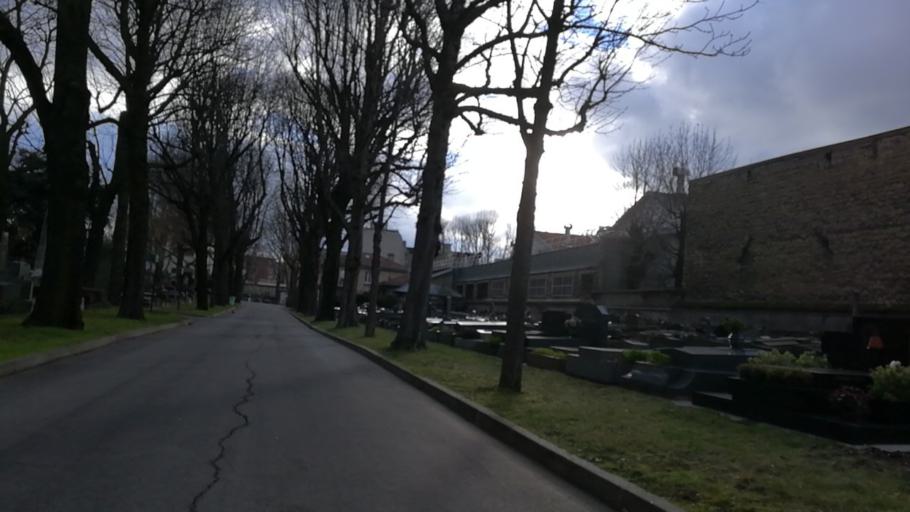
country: FR
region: Ile-de-France
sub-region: Paris
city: Saint-Ouen
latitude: 48.9083
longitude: 2.3466
